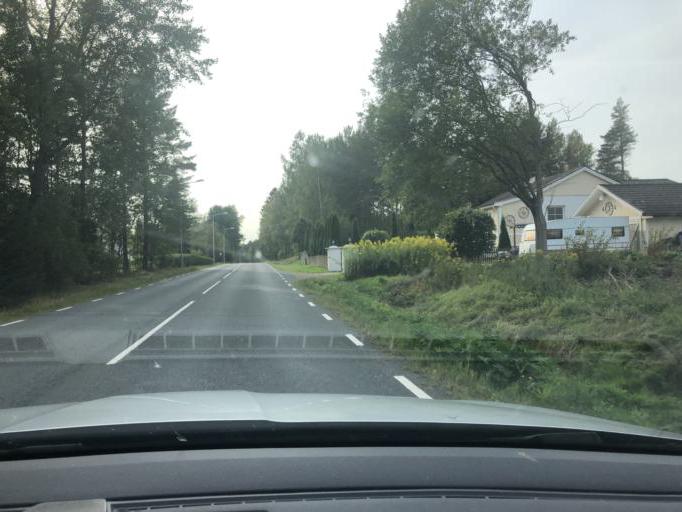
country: SE
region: Joenkoeping
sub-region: Vetlanda Kommun
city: Ekenassjon
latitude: 57.5244
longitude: 14.9231
